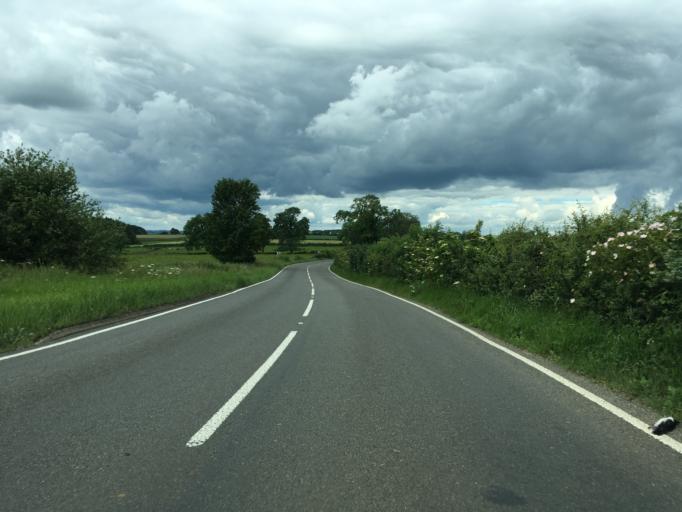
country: GB
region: England
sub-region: Northamptonshire
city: Brackley
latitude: 52.0891
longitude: -1.2080
